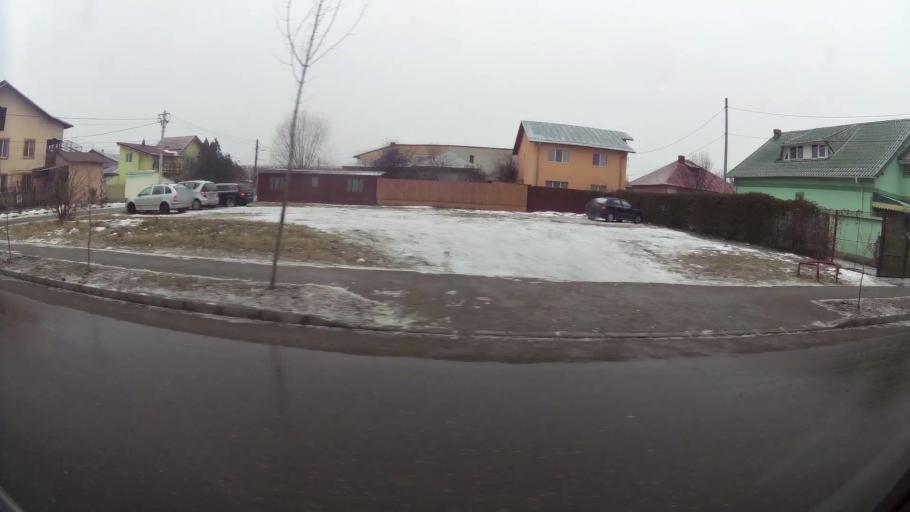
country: RO
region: Prahova
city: Ploiesti
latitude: 44.9515
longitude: 26.0461
